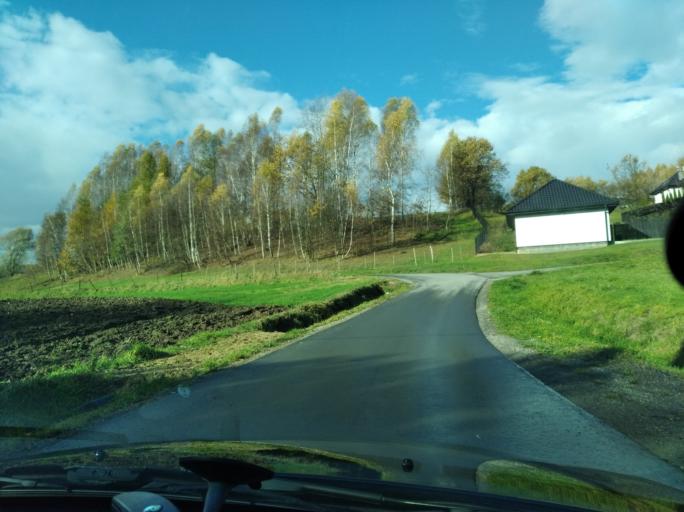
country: PL
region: Subcarpathian Voivodeship
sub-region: Powiat ropczycko-sedziszowski
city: Niedzwiada
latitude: 50.0254
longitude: 21.4809
